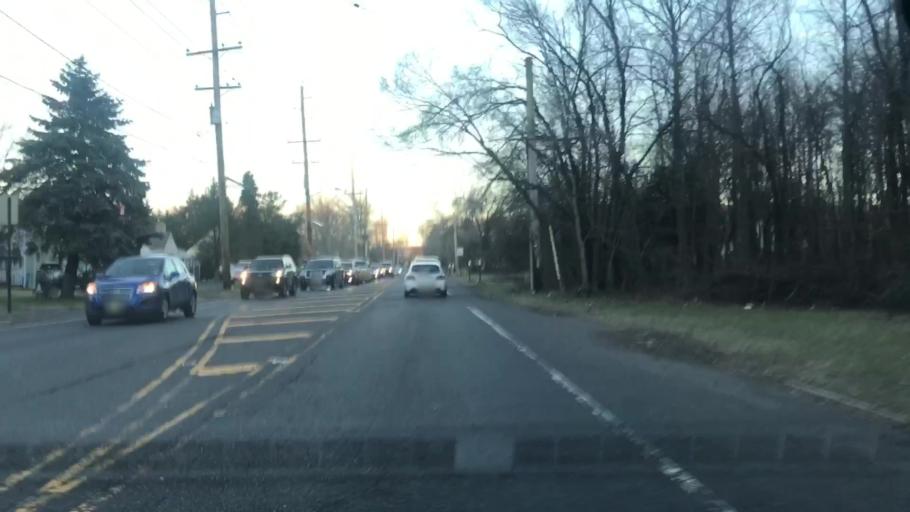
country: US
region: New Jersey
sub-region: Burlington County
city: Burlington
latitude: 40.0503
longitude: -74.8502
